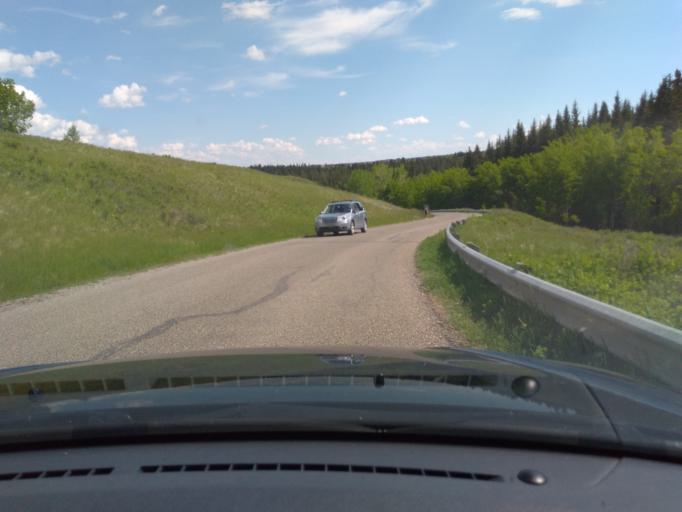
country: CA
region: Alberta
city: Calgary
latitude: 50.9323
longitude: -114.1168
